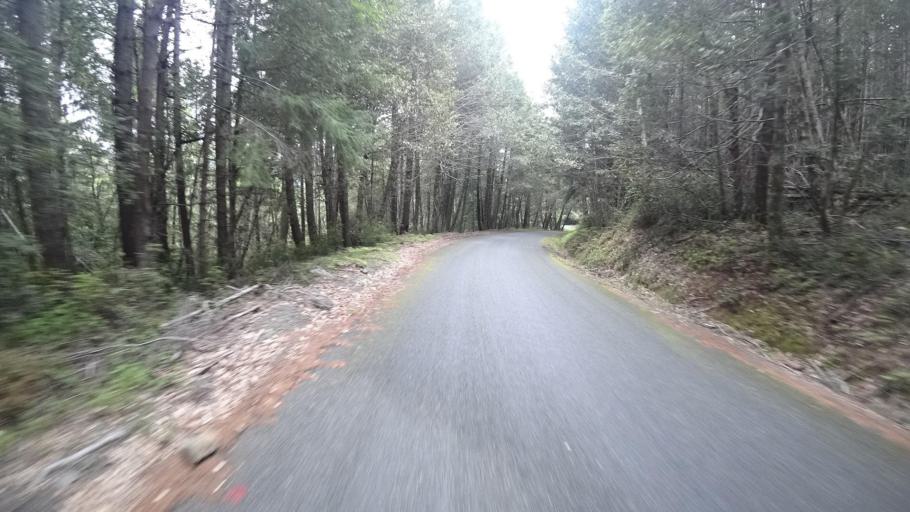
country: US
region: California
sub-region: Humboldt County
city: Willow Creek
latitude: 41.1999
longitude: -123.7706
